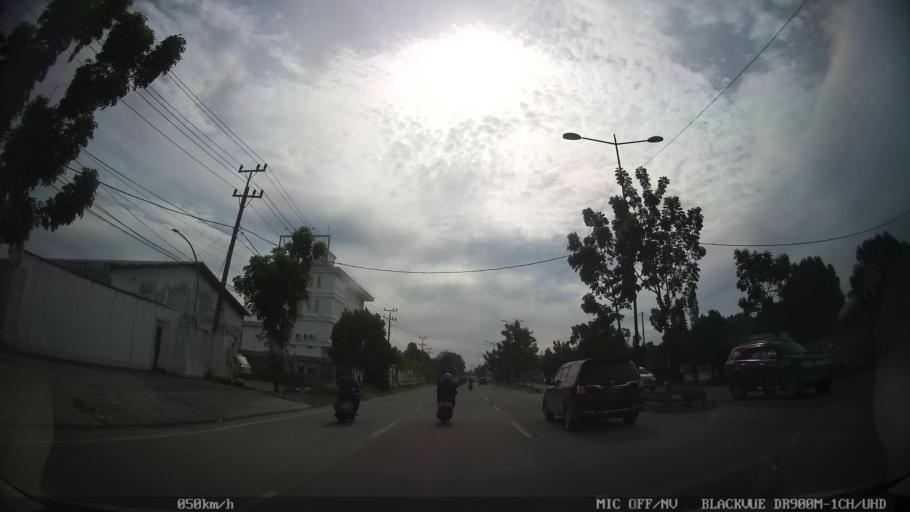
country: ID
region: North Sumatra
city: Medan
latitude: 3.6295
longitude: 98.6895
